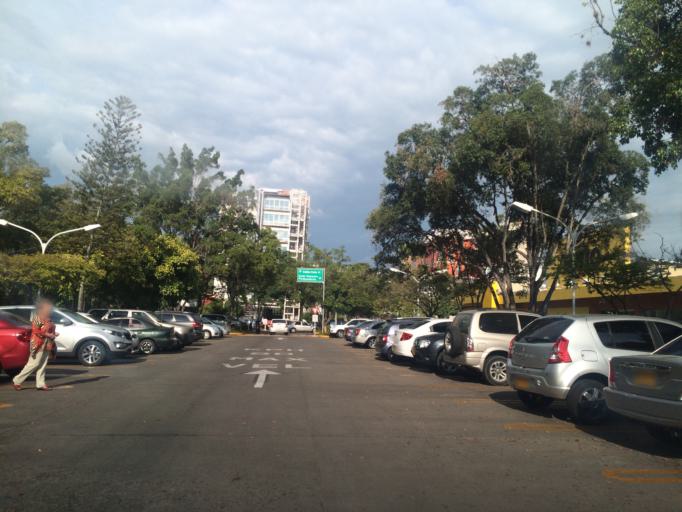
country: CO
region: Valle del Cauca
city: Cali
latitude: 3.3756
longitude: -76.5394
